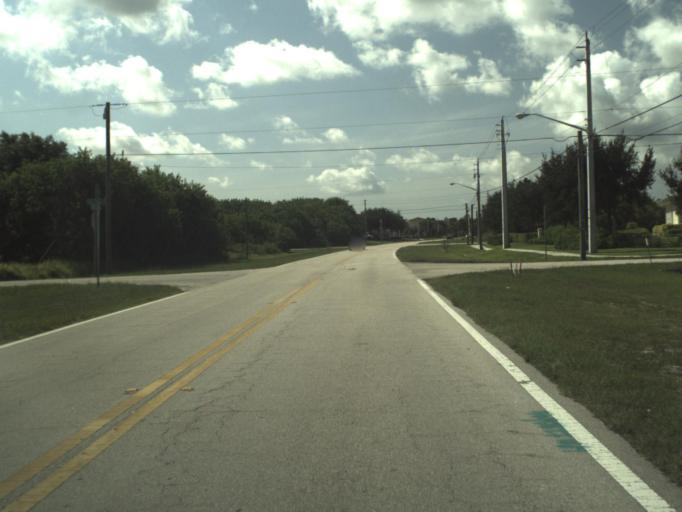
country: US
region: Florida
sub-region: Saint Lucie County
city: Port Saint Lucie
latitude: 27.2302
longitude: -80.3750
